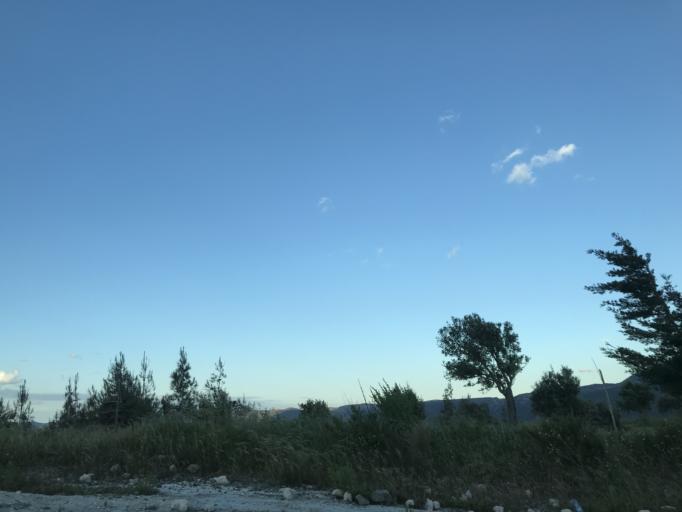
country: TR
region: Hatay
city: Buyukcat
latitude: 36.1097
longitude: 36.0487
